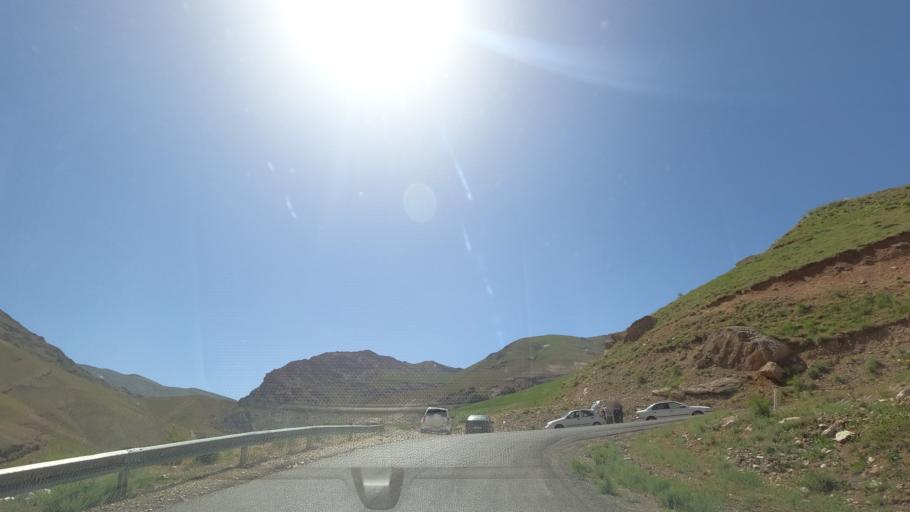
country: IR
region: Alborz
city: Karaj
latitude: 35.9230
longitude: 51.1606
